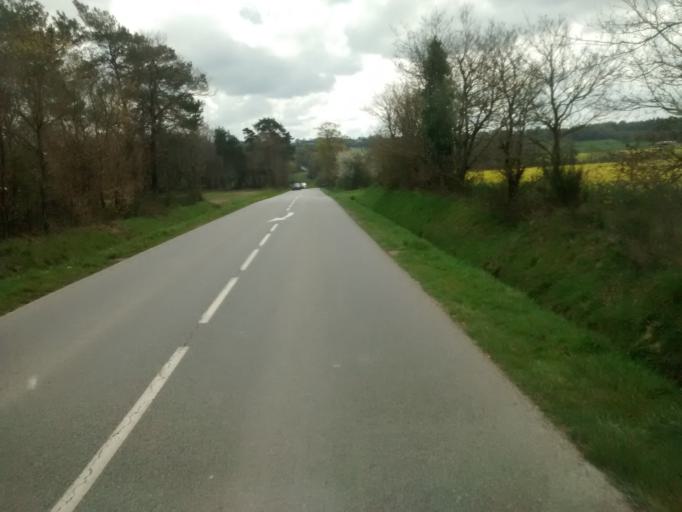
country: FR
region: Brittany
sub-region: Departement du Morbihan
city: Ploermel
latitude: 47.8972
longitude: -2.3679
